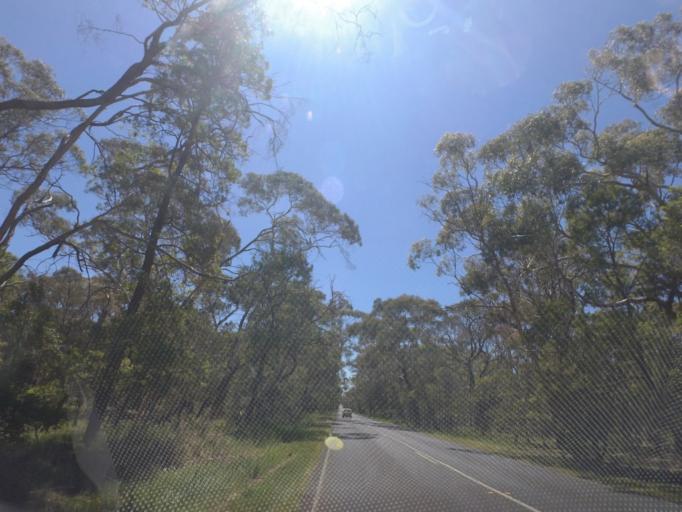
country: AU
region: Victoria
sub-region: Melton
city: Melton West
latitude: -37.5166
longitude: 144.5619
